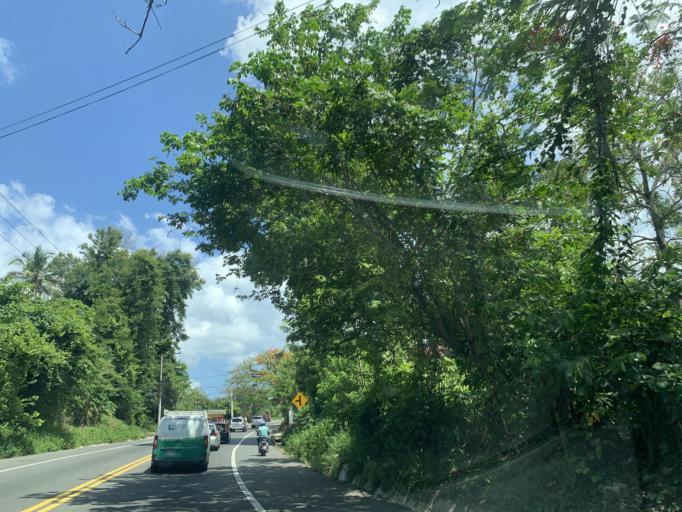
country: DO
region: Puerto Plata
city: Altamira
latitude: 19.6822
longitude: -70.8382
